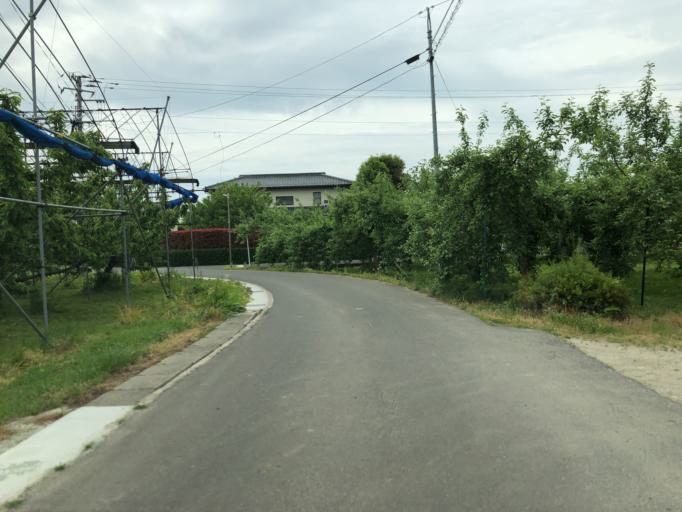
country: JP
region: Fukushima
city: Fukushima-shi
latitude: 37.8157
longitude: 140.4337
